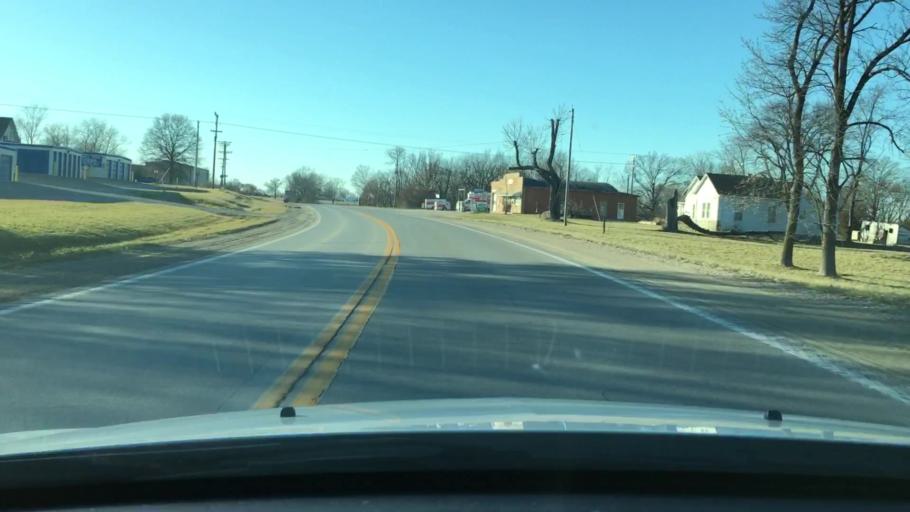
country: US
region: Missouri
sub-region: Audrain County
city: Mexico
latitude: 39.1900
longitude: -91.9809
